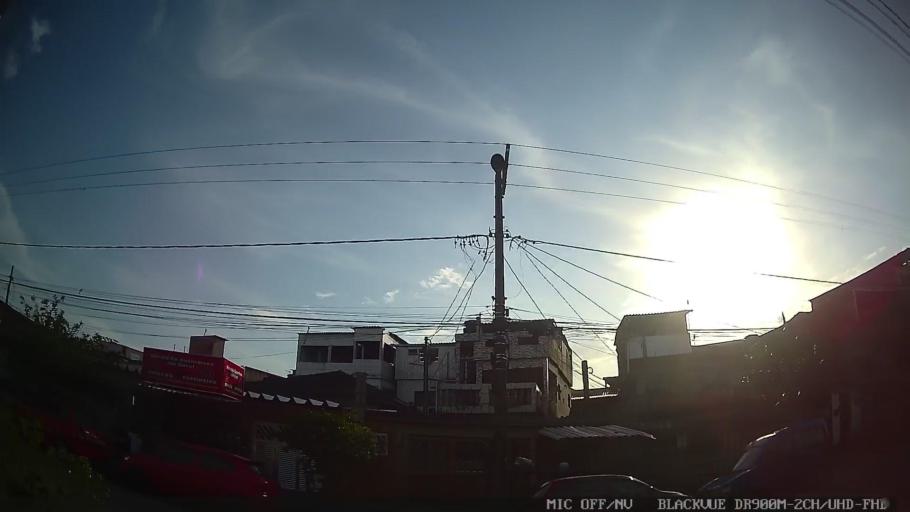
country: BR
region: Sao Paulo
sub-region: Cubatao
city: Cubatao
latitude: -23.9052
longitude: -46.4232
